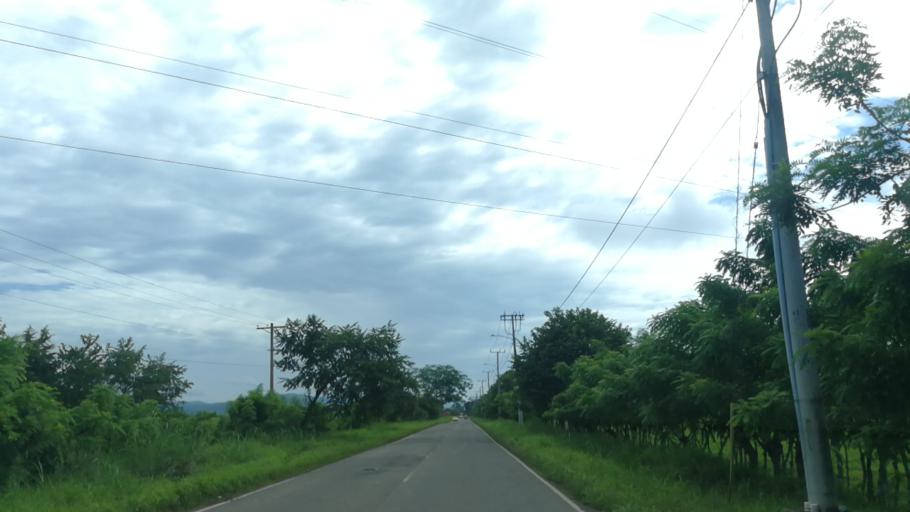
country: PA
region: Panama
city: Los Lotes
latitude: 9.1073
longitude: -79.2692
